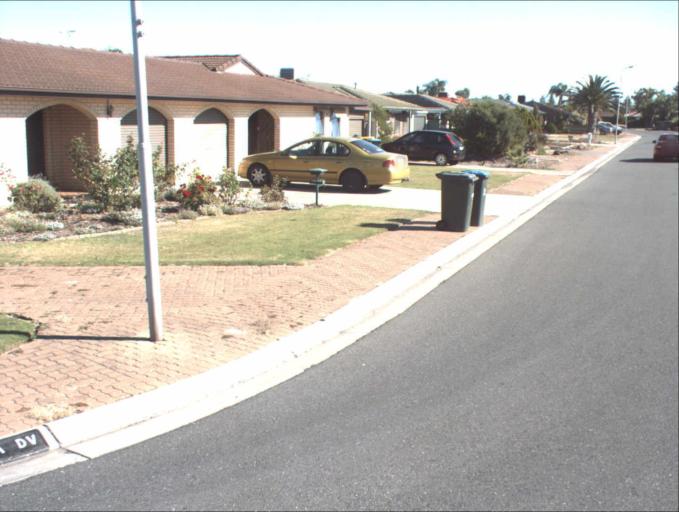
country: AU
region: South Australia
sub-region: Port Adelaide Enfield
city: Birkenhead
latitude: -34.7797
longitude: 138.4937
